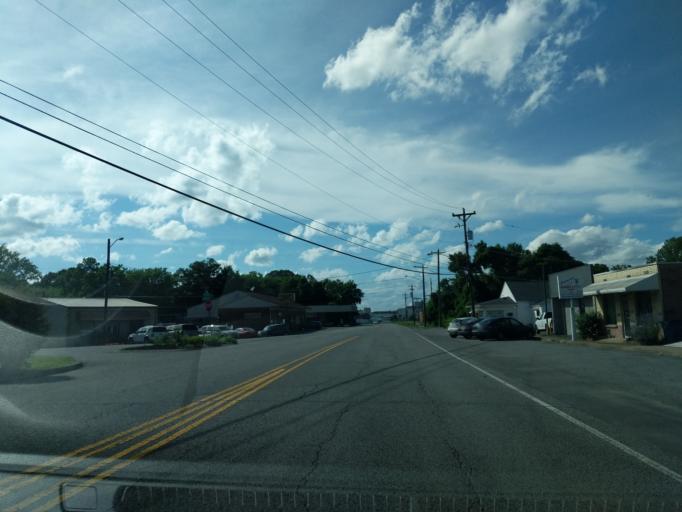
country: US
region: Tennessee
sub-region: Davidson County
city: Lakewood
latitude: 36.2647
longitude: -86.6504
